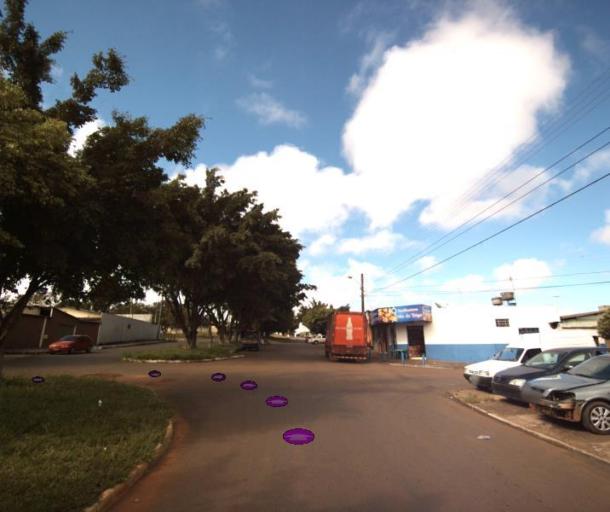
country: BR
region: Goias
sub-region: Anapolis
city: Anapolis
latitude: -16.2846
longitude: -48.9570
